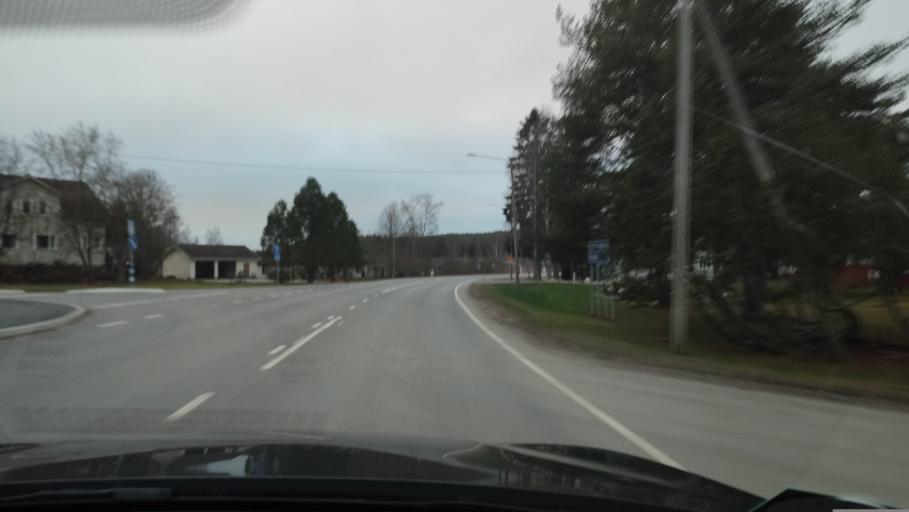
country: FI
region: Southern Ostrobothnia
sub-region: Suupohja
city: Karijoki
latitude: 62.3061
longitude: 21.7009
